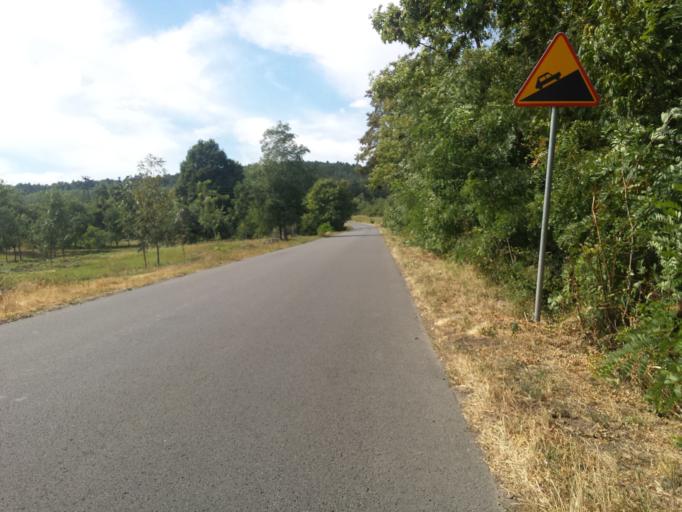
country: PL
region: Subcarpathian Voivodeship
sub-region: Powiat przemyski
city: Fredropol
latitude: 49.6720
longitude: 22.7342
